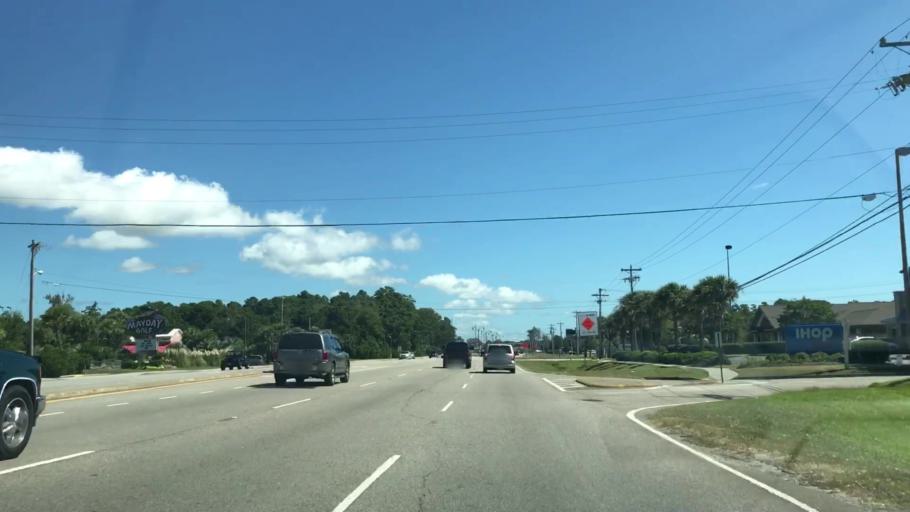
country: US
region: South Carolina
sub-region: Horry County
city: North Myrtle Beach
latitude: 33.8338
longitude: -78.6729
